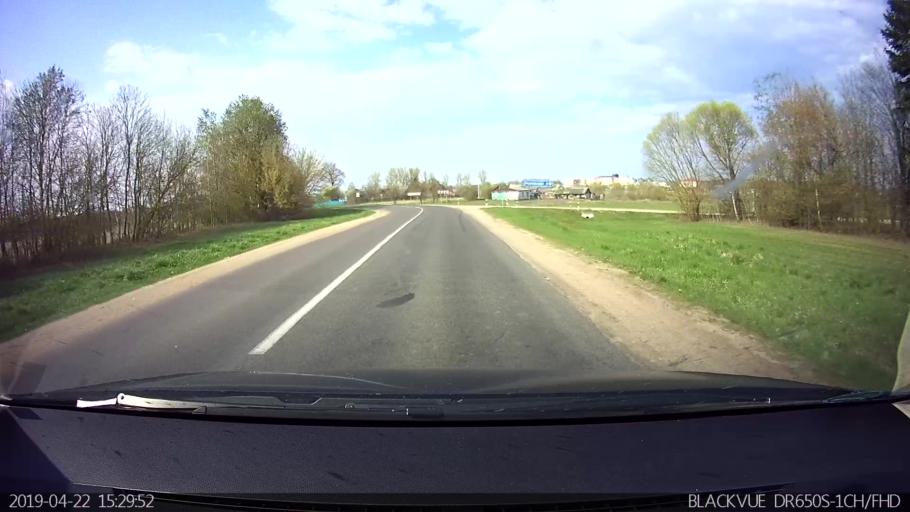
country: BY
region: Brest
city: Vysokaye
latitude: 52.3930
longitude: 23.3756
